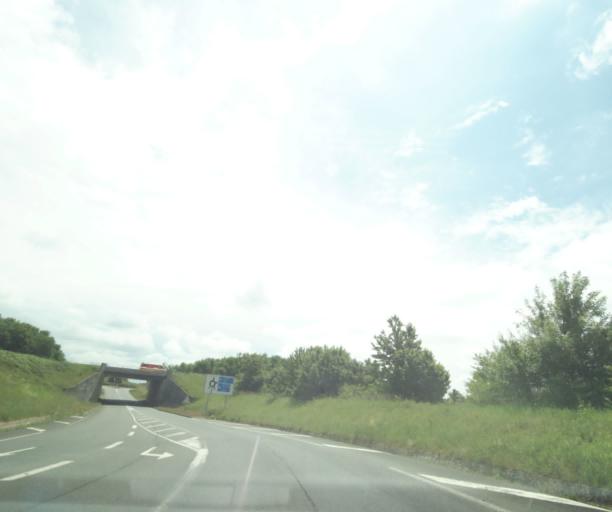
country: FR
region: Poitou-Charentes
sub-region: Departement des Deux-Sevres
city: Echire
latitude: 46.4238
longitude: -0.3986
